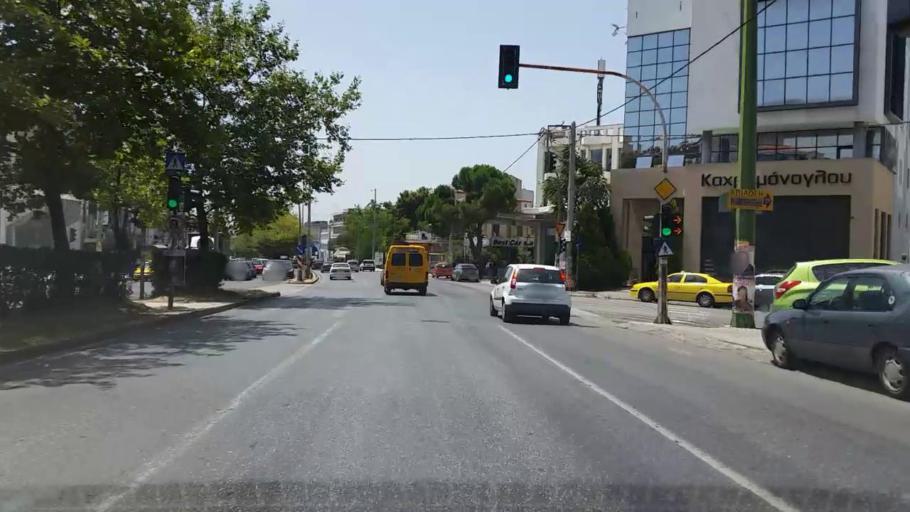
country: GR
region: Attica
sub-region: Nomarchia Athinas
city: Agia Paraskevi
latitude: 38.0138
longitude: 23.8311
